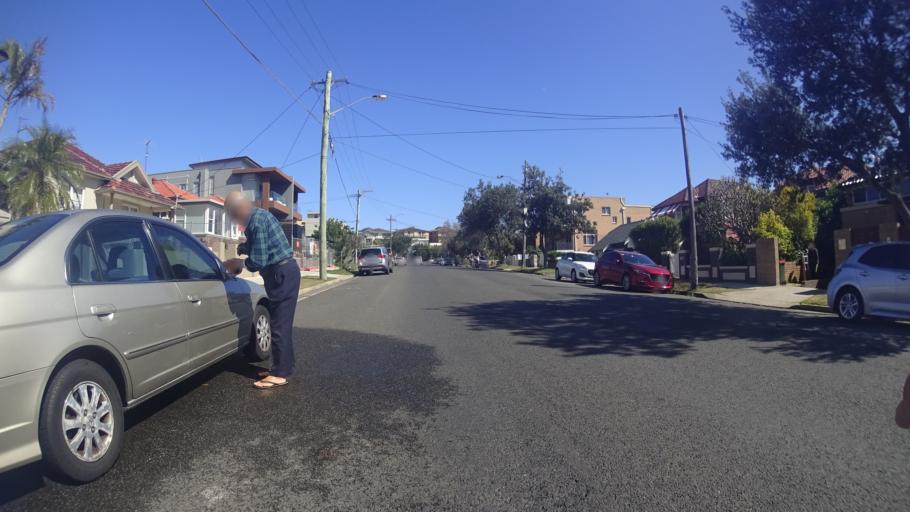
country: AU
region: New South Wales
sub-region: Randwick
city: South Coogee
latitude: -33.9400
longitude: 151.2585
